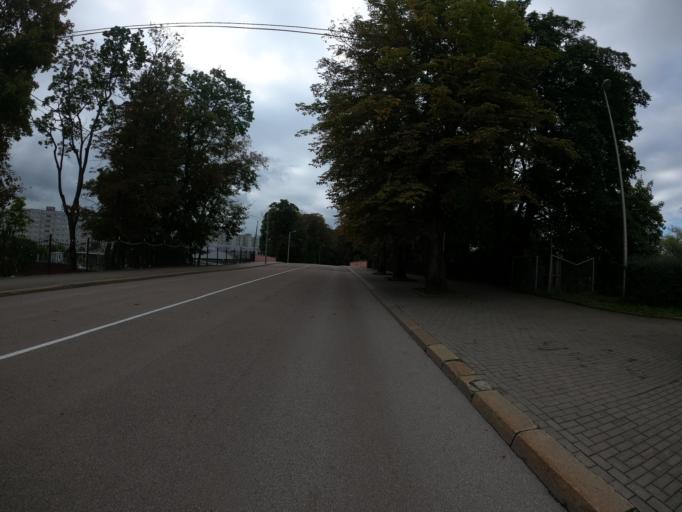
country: RU
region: Kaliningrad
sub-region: Gorod Kaliningrad
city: Kaliningrad
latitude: 54.7107
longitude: 20.4906
